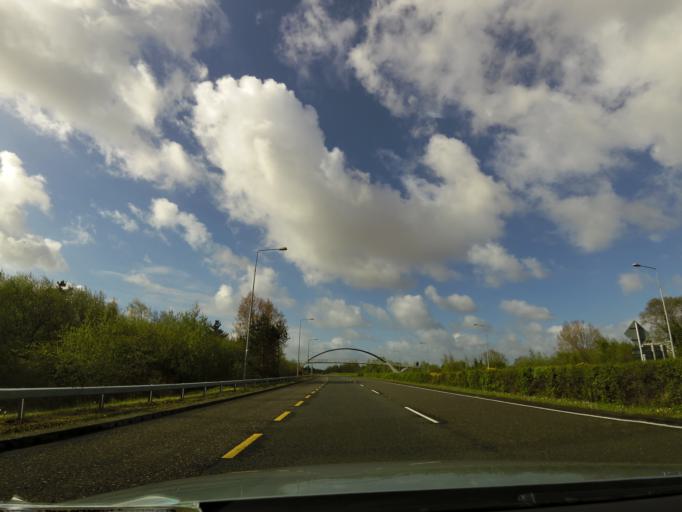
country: IE
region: Munster
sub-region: An Clar
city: Shannon
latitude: 52.7110
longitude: -8.8872
